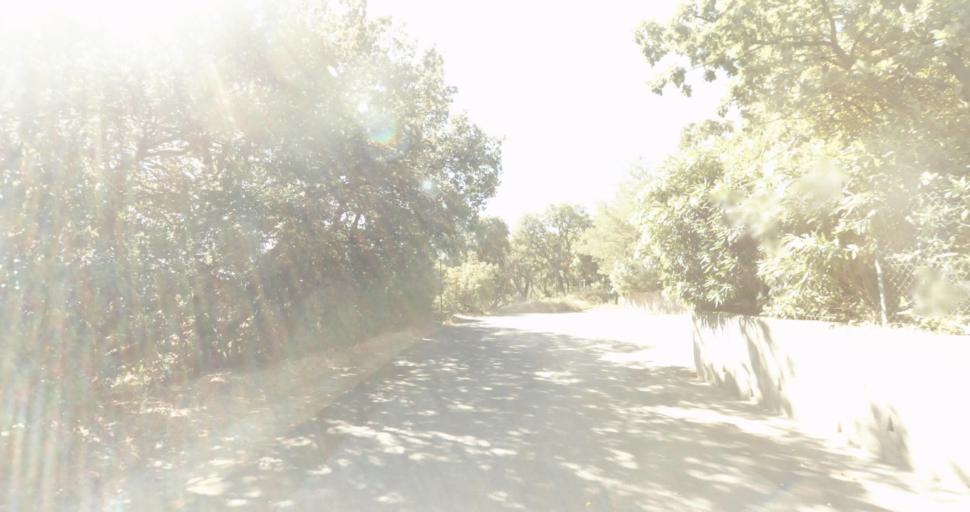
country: FR
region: Provence-Alpes-Cote d'Azur
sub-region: Departement du Var
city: Saint-Tropez
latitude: 43.2593
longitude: 6.6132
